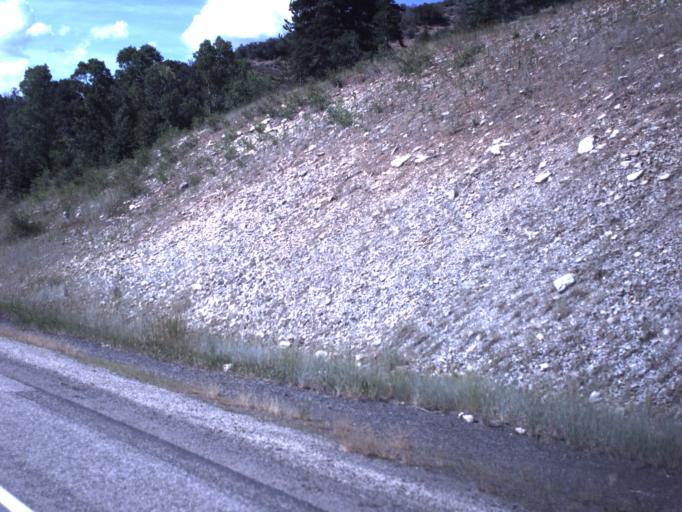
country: US
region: Utah
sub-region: Wasatch County
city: Heber
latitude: 40.3389
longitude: -111.2622
